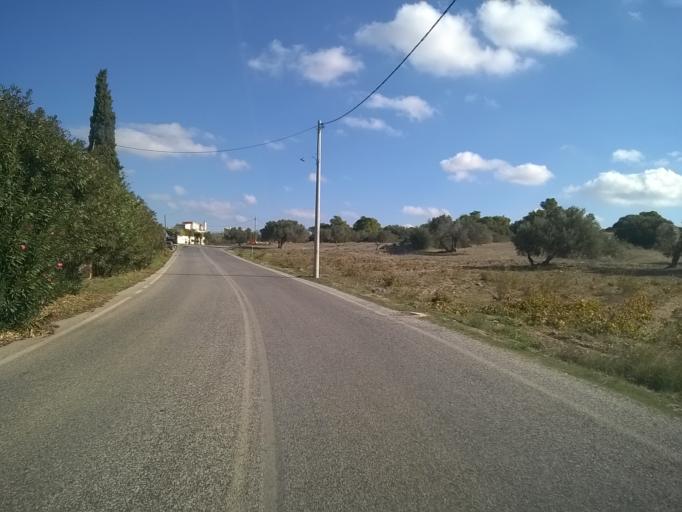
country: GR
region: Attica
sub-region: Nomarchia Anatolikis Attikis
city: Anavyssos
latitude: 37.7538
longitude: 23.9604
